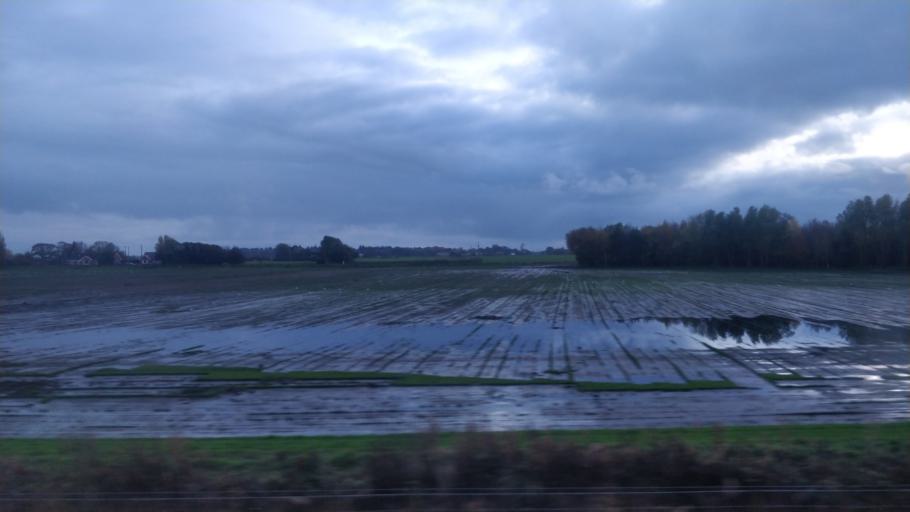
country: GB
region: England
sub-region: Lancashire
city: Ormskirk
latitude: 53.6217
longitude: -2.9061
